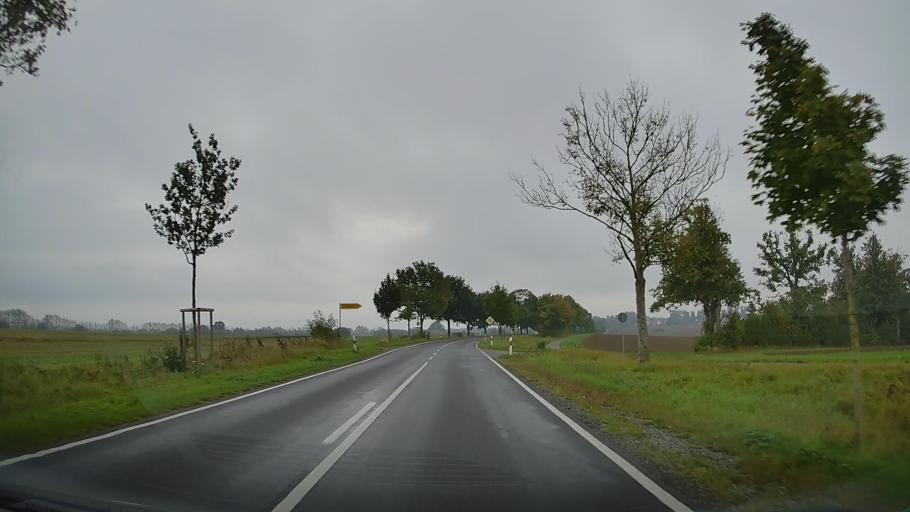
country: DE
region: Mecklenburg-Vorpommern
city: Ostseebad Boltenhagen
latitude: 53.9520
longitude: 11.2293
